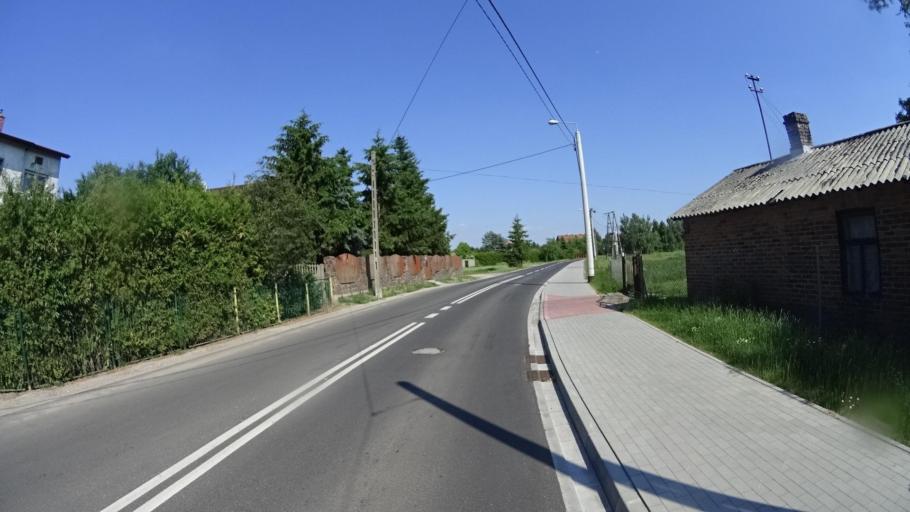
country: PL
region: Masovian Voivodeship
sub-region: Powiat warszawski zachodni
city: Blonie
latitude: 52.1691
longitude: 20.6192
